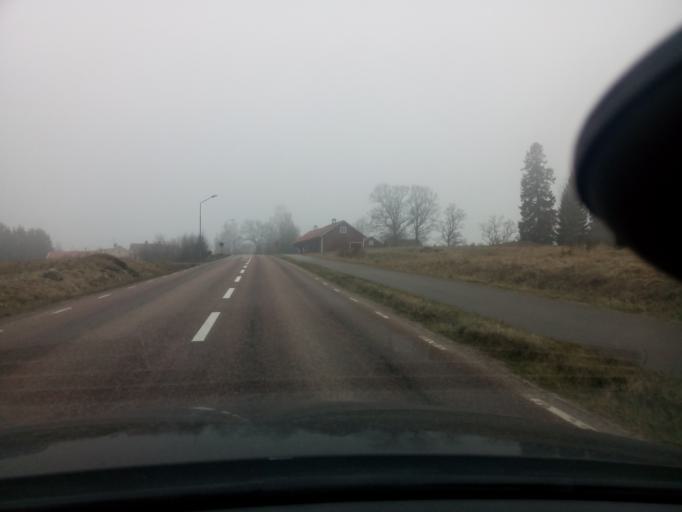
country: SE
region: Soedermanland
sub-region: Nykopings Kommun
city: Nykoping
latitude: 58.8699
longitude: 17.0709
